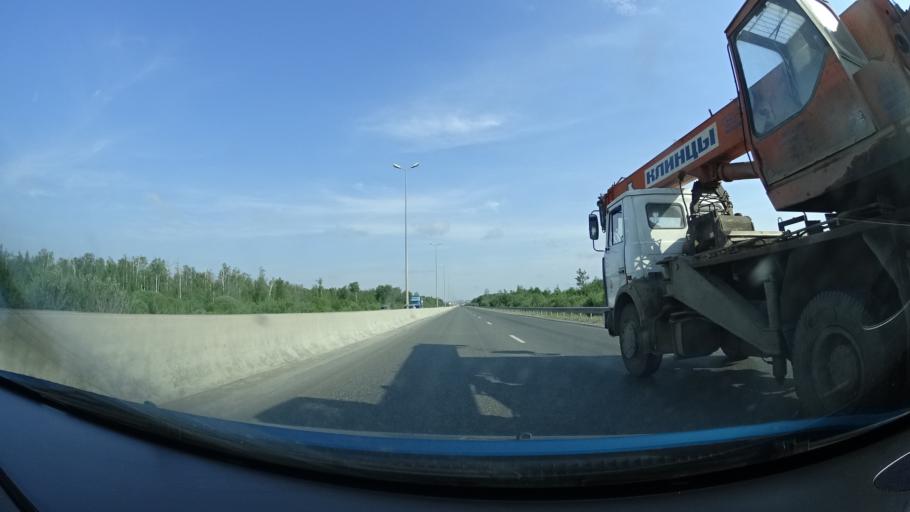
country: RU
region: Perm
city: Kondratovo
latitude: 57.9911
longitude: 56.0642
